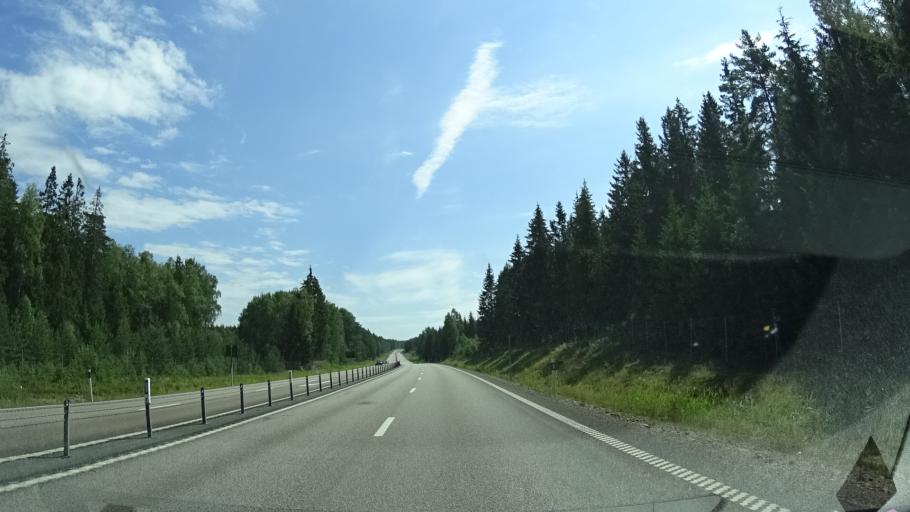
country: SE
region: Vaermland
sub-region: Kristinehamns Kommun
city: Kristinehamn
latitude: 59.3601
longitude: 14.0364
